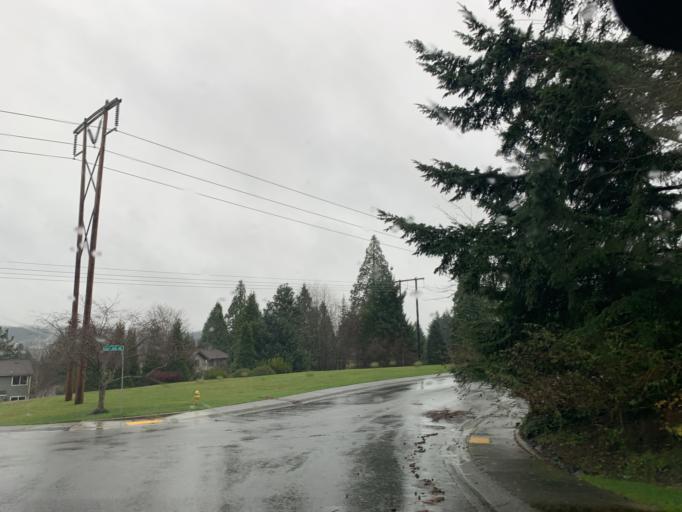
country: US
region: Washington
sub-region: King County
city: Woodinville
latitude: 47.7348
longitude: -122.1608
